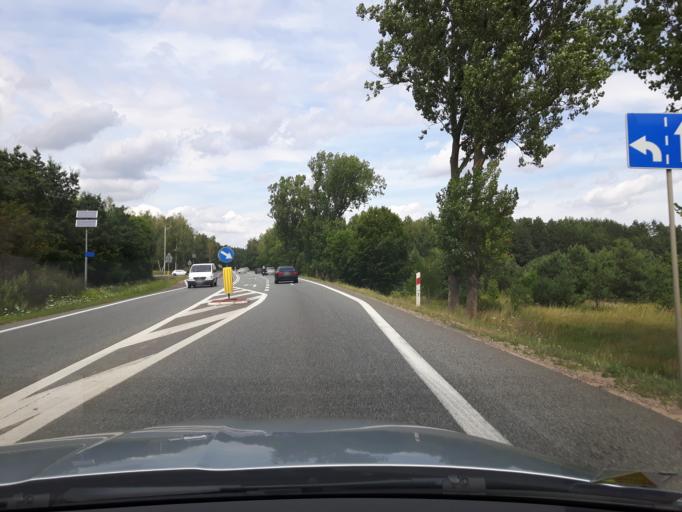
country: PL
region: Masovian Voivodeship
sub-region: Powiat mlawski
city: Mlawa
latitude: 53.1316
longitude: 20.3952
